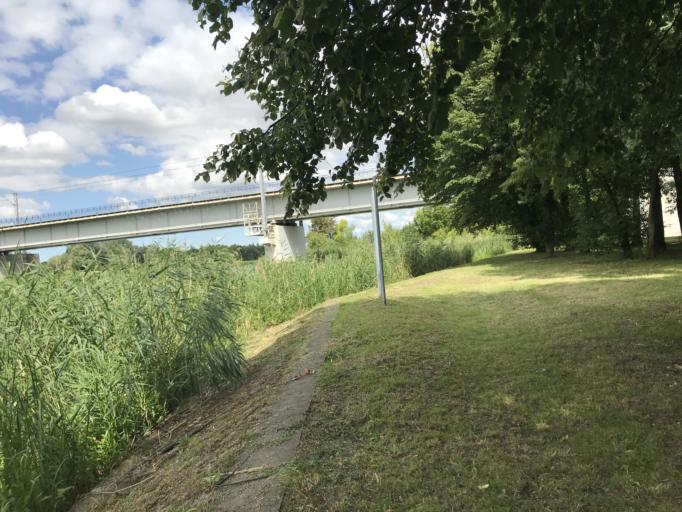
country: PL
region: Pomeranian Voivodeship
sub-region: Powiat malborski
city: Malbork
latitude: 54.0431
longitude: 19.0303
